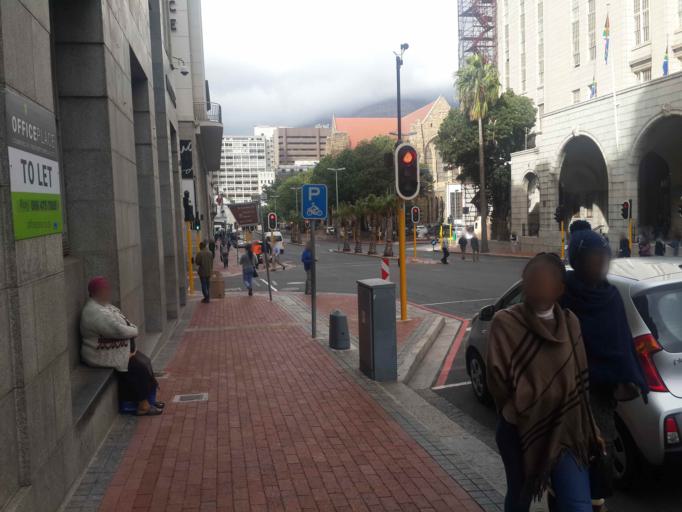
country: ZA
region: Western Cape
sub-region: City of Cape Town
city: Cape Town
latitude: -33.9238
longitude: 18.4185
